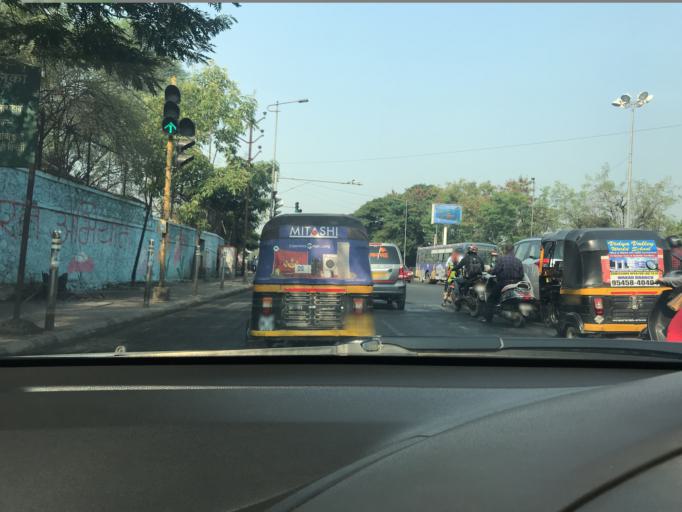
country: IN
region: Maharashtra
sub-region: Pune Division
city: Khadki
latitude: 18.5498
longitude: 73.8099
